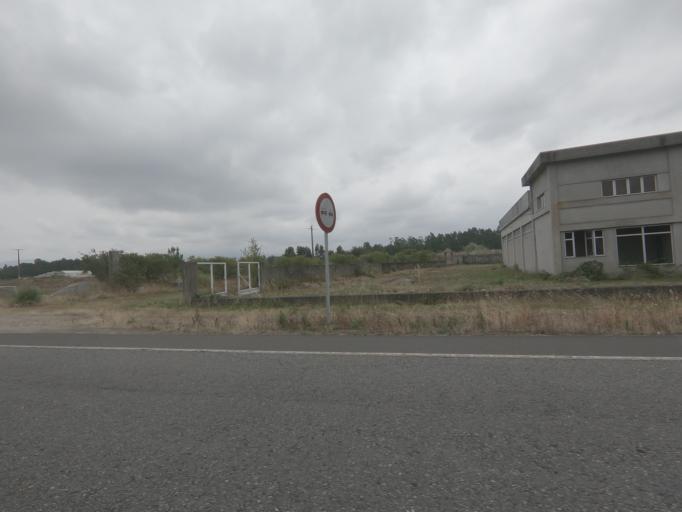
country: ES
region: Galicia
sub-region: Provincia de Pontevedra
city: Tomino
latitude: 41.9888
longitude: -8.7153
